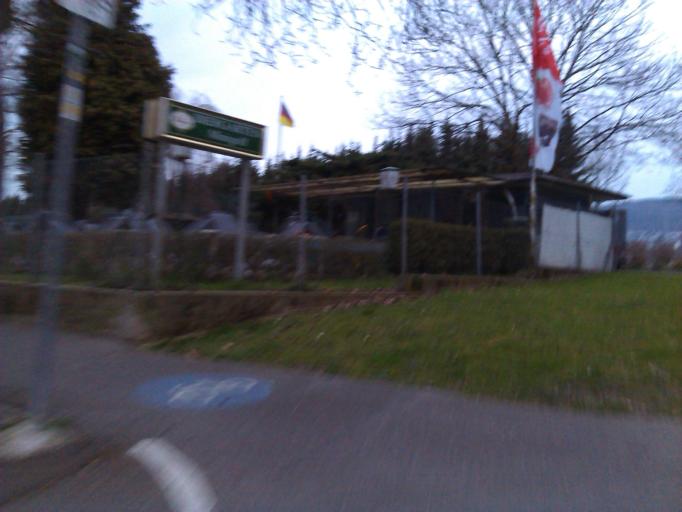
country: DE
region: Rheinland-Pfalz
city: Lahnstein
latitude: 50.3108
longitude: 7.5940
